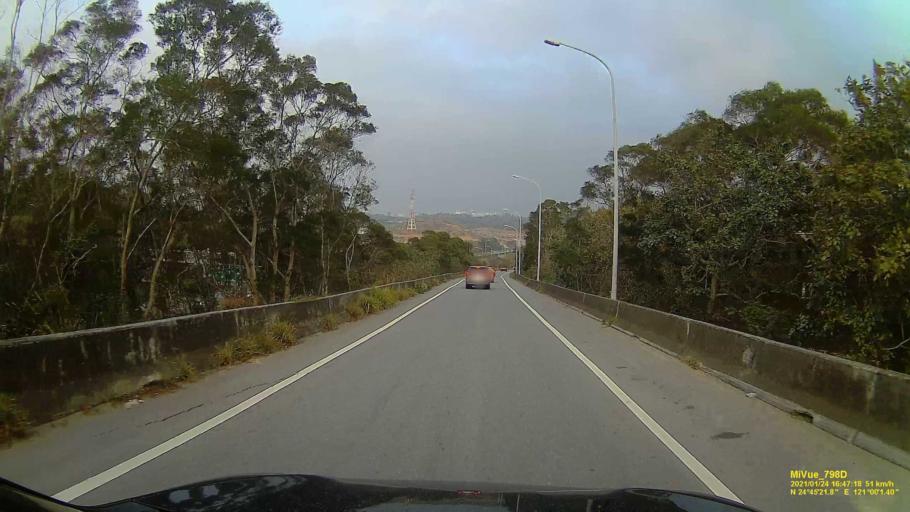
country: TW
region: Taiwan
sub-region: Hsinchu
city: Hsinchu
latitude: 24.7562
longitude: 121.0008
